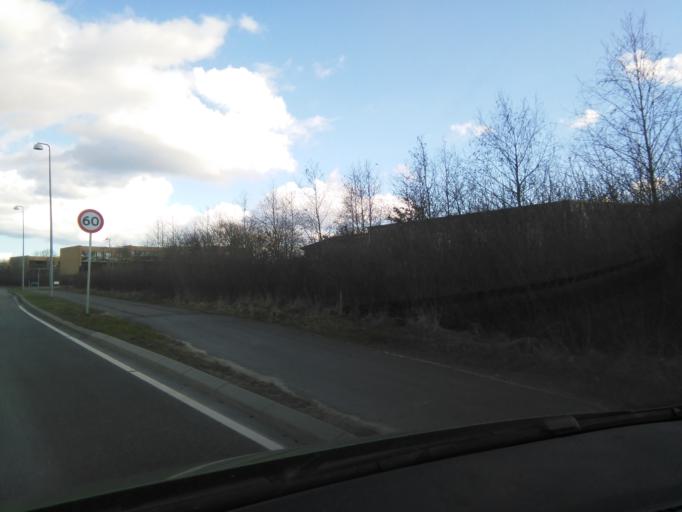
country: DK
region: Central Jutland
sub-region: Silkeborg Kommune
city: Silkeborg
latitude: 56.1881
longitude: 9.5022
